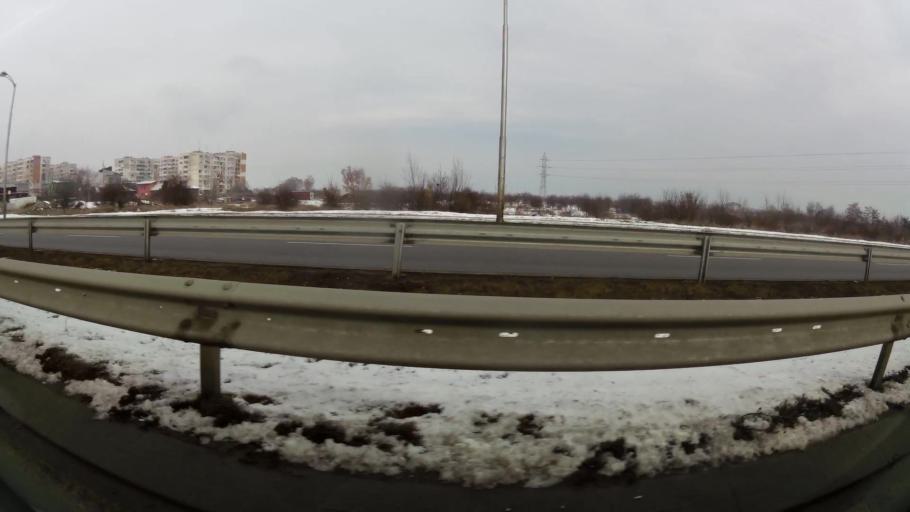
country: BG
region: Sofia-Capital
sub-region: Stolichna Obshtina
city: Sofia
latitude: 42.7098
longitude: 23.3908
